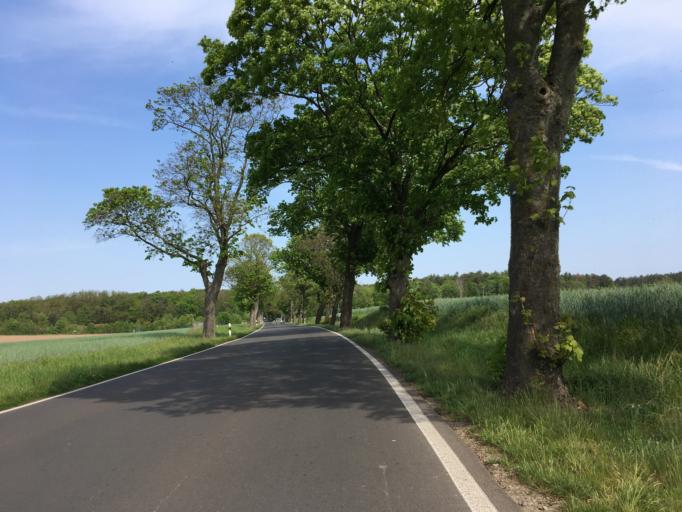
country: DE
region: Brandenburg
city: Werneuchen
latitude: 52.6096
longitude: 13.7573
